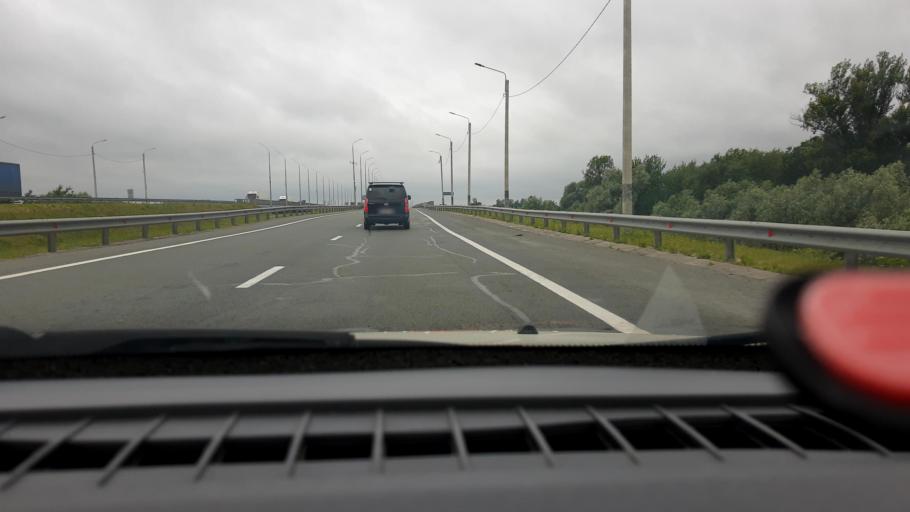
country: RU
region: Vladimir
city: Galitsy
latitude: 56.2232
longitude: 42.7845
